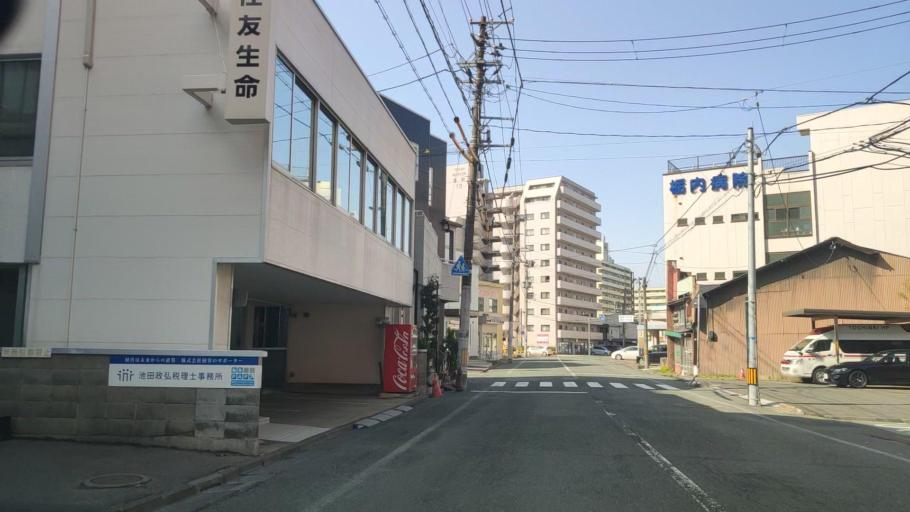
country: JP
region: Iwate
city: Morioka-shi
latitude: 39.6986
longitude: 141.1538
